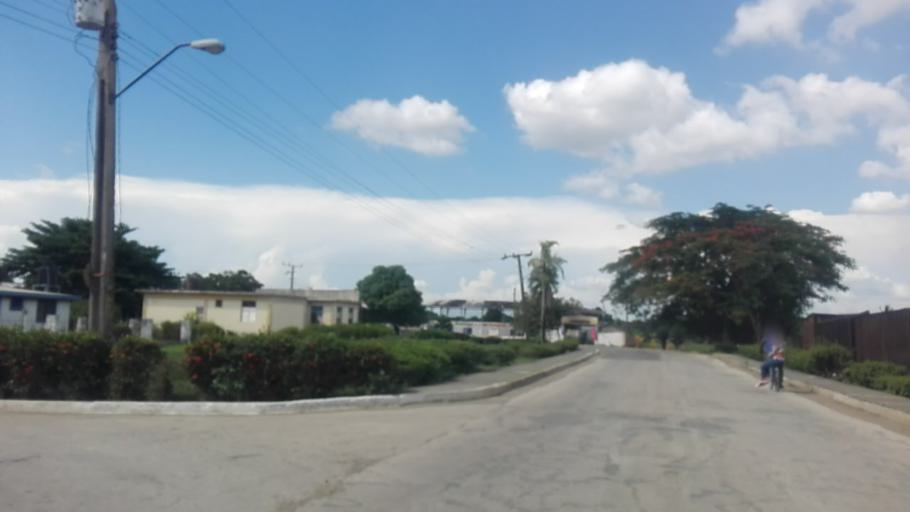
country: CU
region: Granma
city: Bartolome Maso
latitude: 20.1677
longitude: -76.9446
